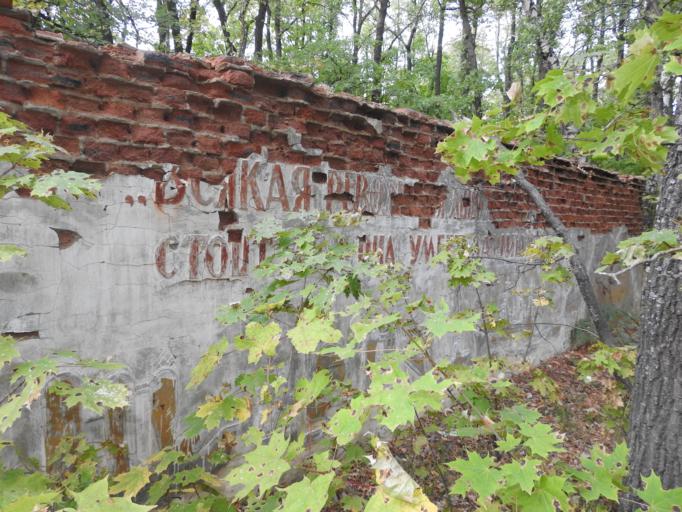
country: RU
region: Saratov
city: Sokolovyy
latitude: 51.5527
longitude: 45.8664
